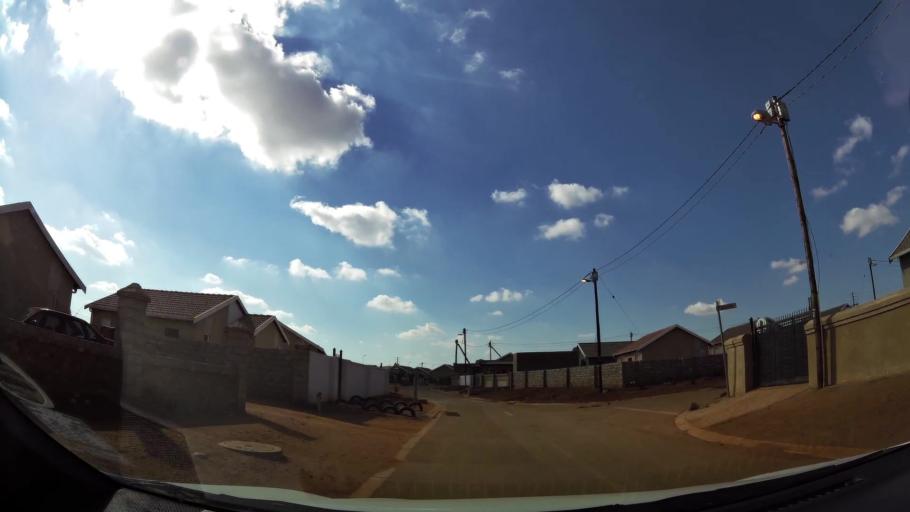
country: ZA
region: Gauteng
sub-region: City of Tshwane Metropolitan Municipality
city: Cullinan
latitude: -25.6864
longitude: 28.4068
